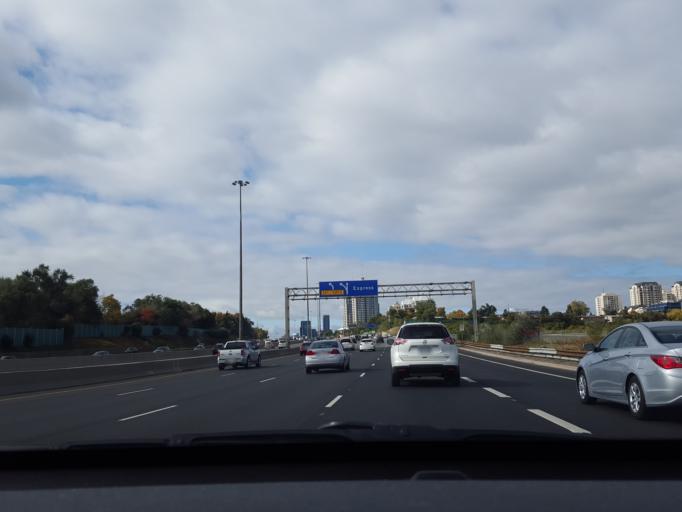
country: CA
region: Ontario
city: Willowdale
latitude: 43.7663
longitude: -79.3696
